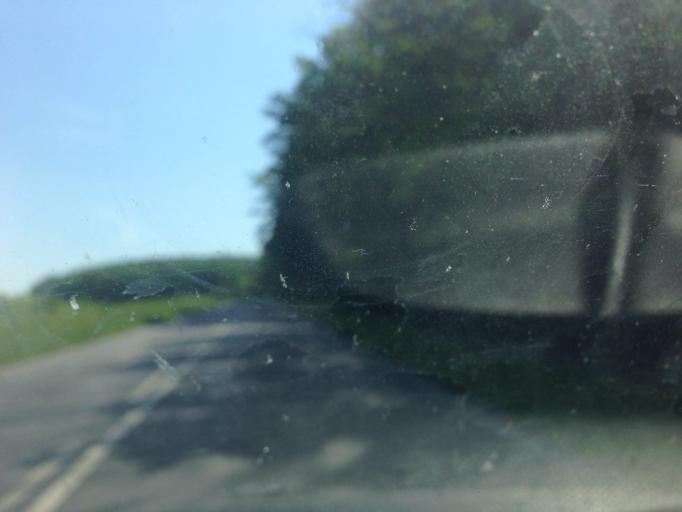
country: PL
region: Pomeranian Voivodeship
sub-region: Powiat tczewski
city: Pelplin
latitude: 53.9272
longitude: 18.6499
